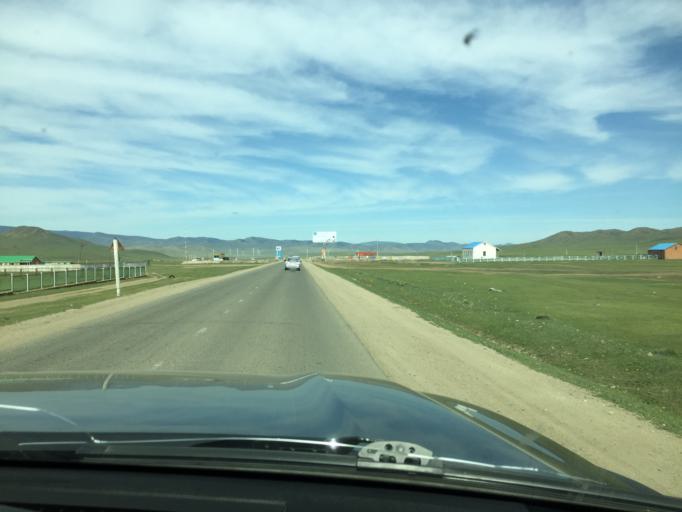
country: MN
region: Central Aimak
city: Ihsueuej
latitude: 48.2274
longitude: 106.2881
